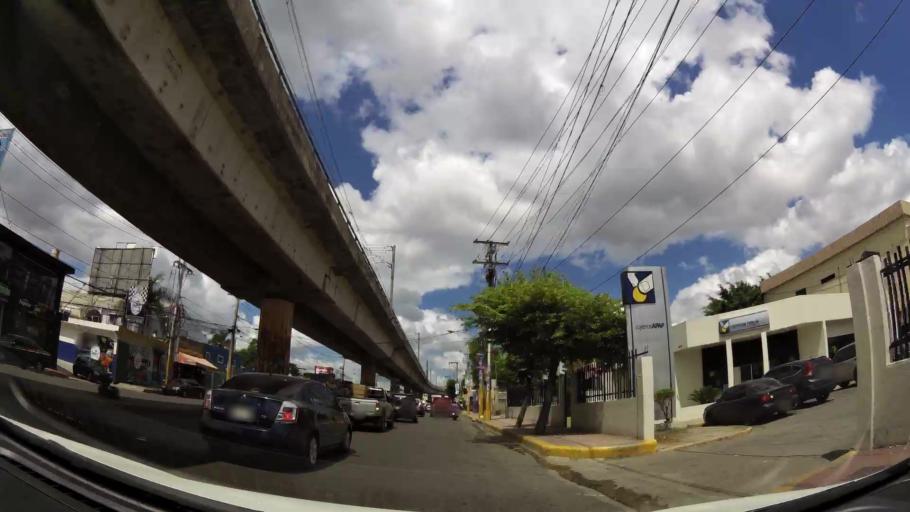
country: DO
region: Nacional
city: Ensanche Luperon
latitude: 18.5204
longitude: -69.9156
